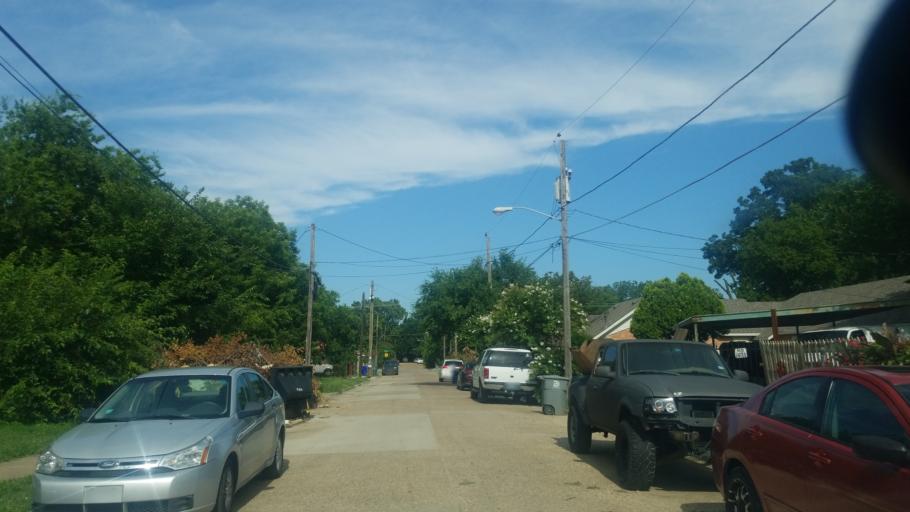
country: US
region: Texas
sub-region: Dallas County
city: Dallas
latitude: 32.7794
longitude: -96.8522
